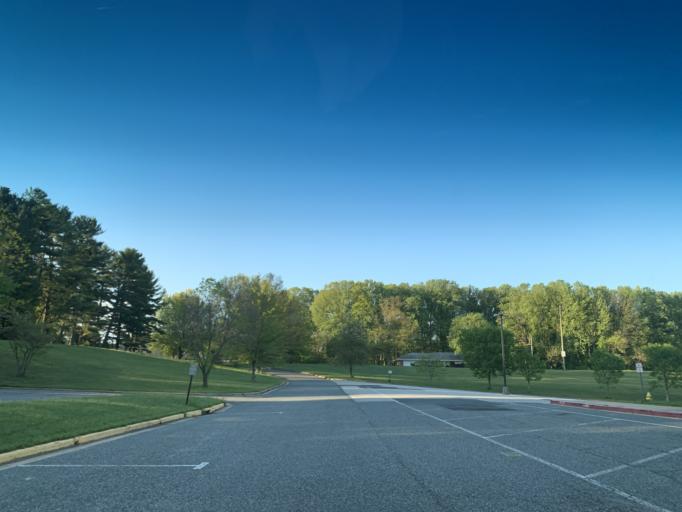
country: US
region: Maryland
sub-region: Harford County
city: Aberdeen
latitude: 39.5158
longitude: -76.1652
